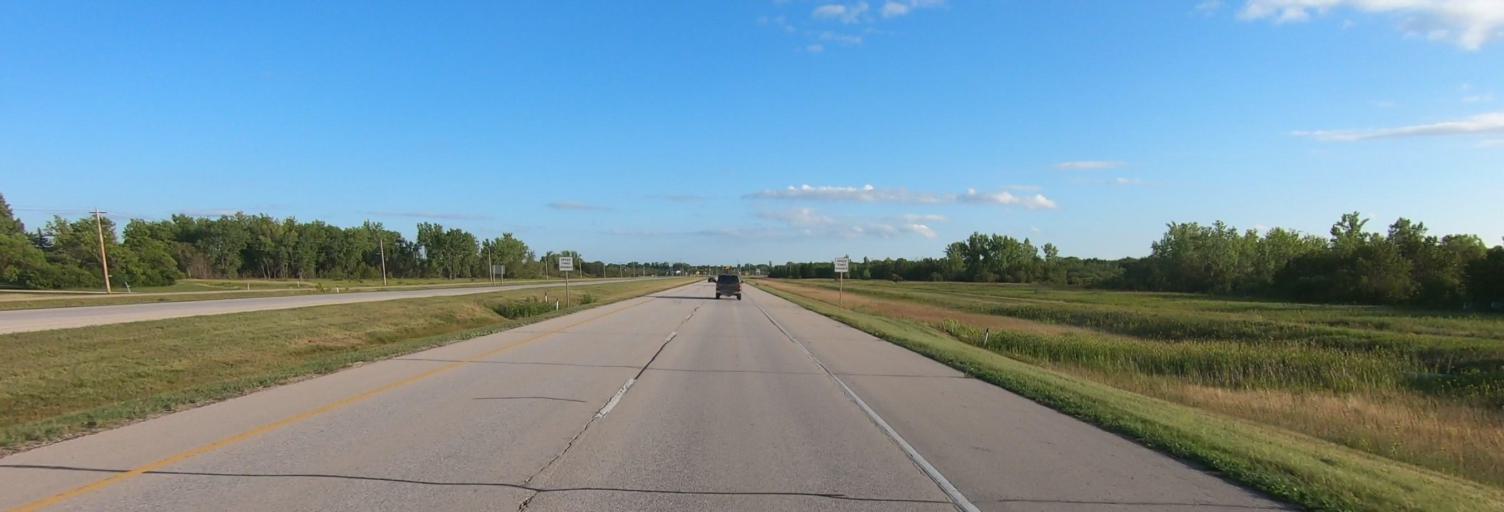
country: CA
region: Manitoba
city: Selkirk
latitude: 49.9810
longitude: -96.9746
